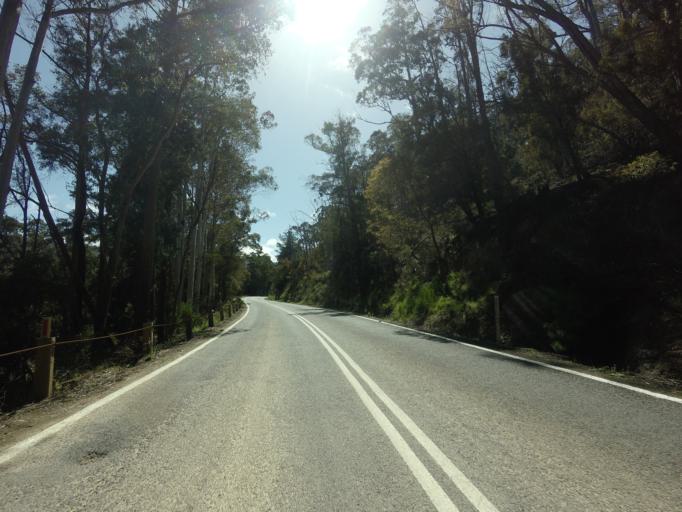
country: AU
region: Tasmania
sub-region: Derwent Valley
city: New Norfolk
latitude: -42.6932
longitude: 146.7146
